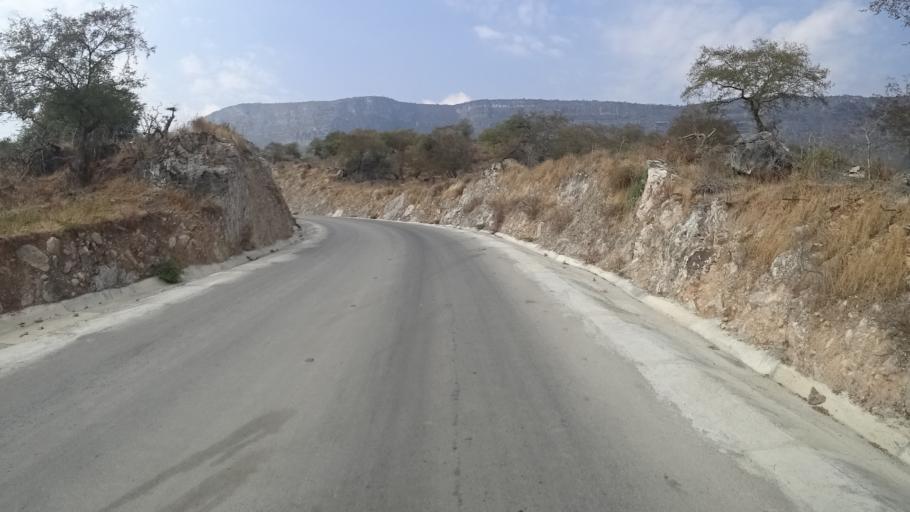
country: YE
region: Al Mahrah
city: Hawf
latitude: 16.7112
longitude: 53.2547
